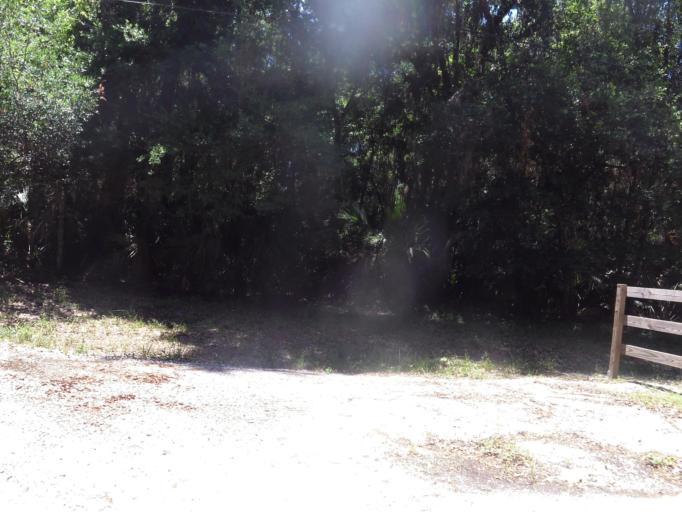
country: US
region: Florida
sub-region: Duval County
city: Atlantic Beach
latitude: 30.4445
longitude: -81.4638
